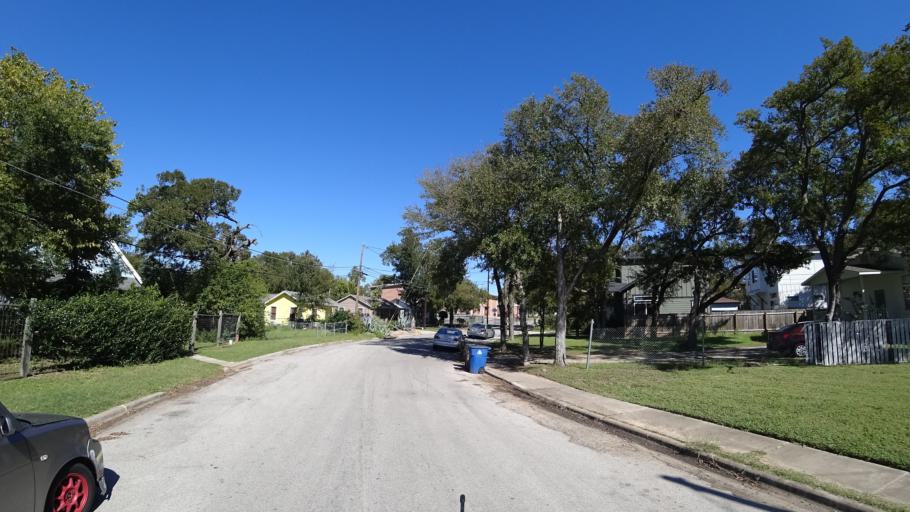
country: US
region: Texas
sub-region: Travis County
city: Austin
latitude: 30.2769
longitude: -97.7066
